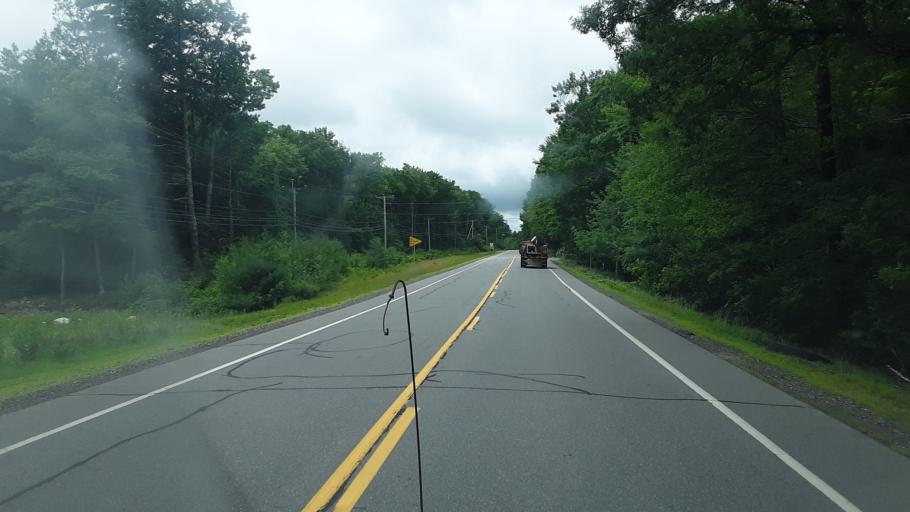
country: US
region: New Hampshire
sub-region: Rockingham County
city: Northwood
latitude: 43.1806
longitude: -71.1094
